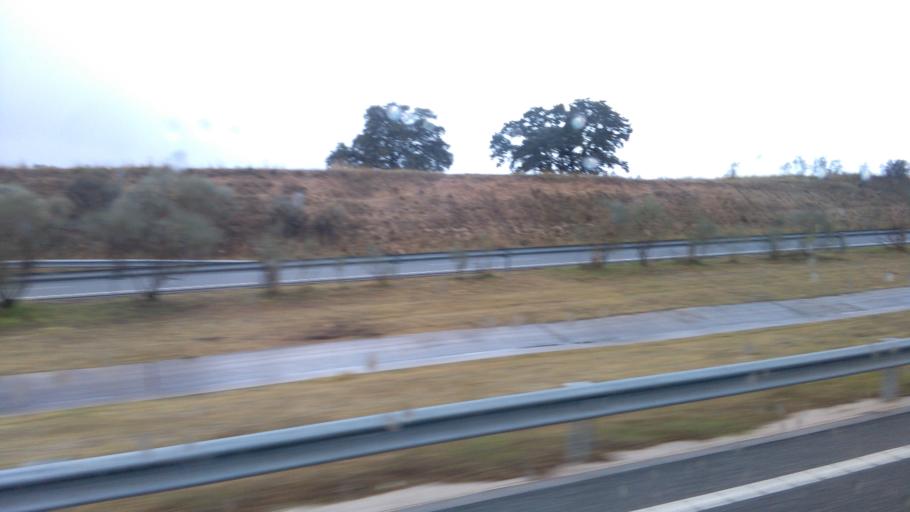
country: ES
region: Madrid
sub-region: Provincia de Madrid
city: Arroyomolinos
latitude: 40.2612
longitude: -3.9614
